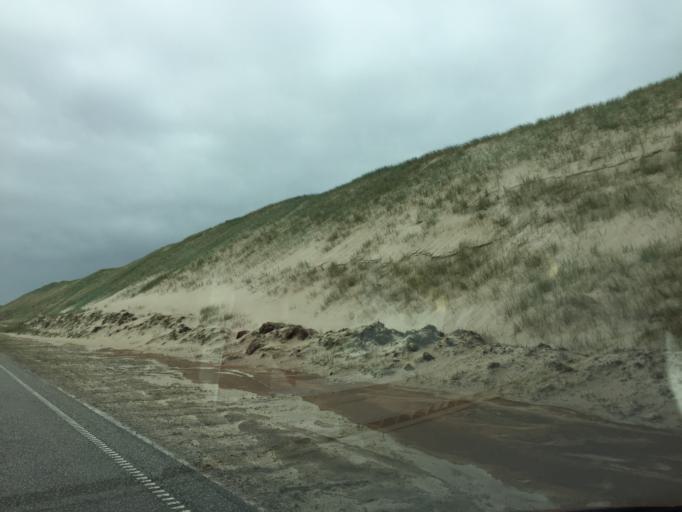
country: DK
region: Central Jutland
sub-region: Lemvig Kommune
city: Harboore
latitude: 56.4422
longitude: 8.1249
